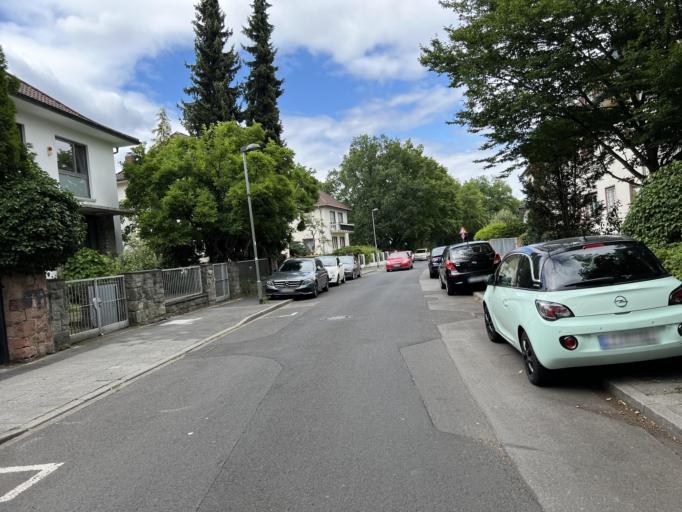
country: DE
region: Hesse
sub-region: Regierungsbezirk Darmstadt
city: Offenbach
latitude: 50.0951
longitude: 8.7499
